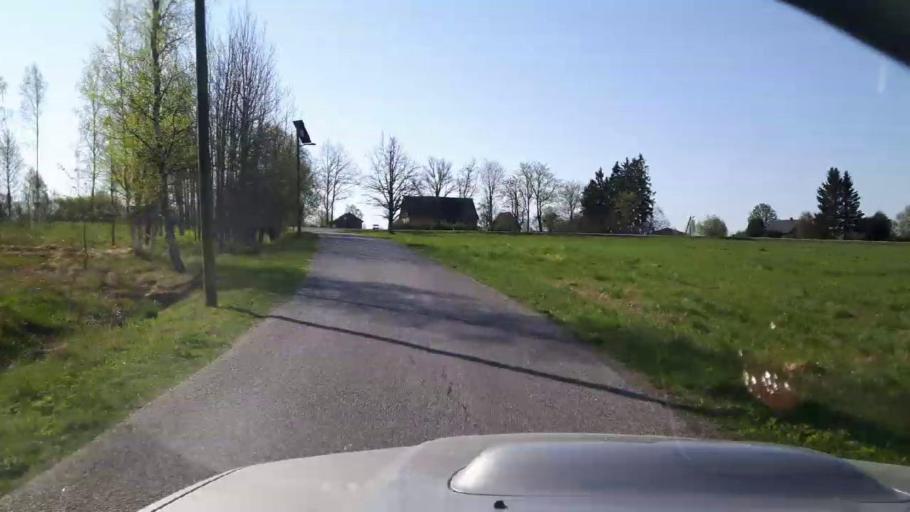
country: EE
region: Paernumaa
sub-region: Sindi linn
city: Sindi
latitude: 58.4482
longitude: 24.7686
